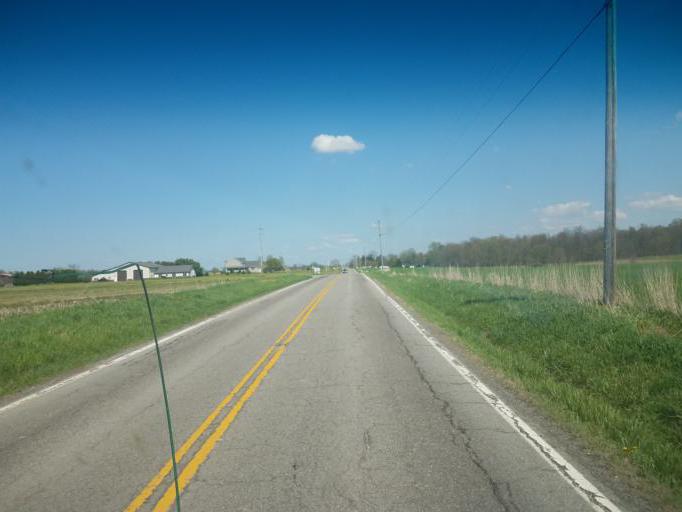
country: US
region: Ohio
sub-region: Wayne County
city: West Salem
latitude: 40.9213
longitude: -82.0883
